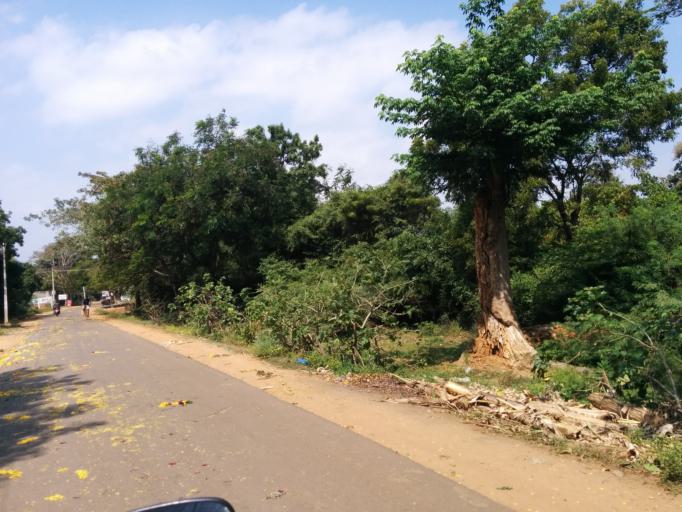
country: IN
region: Tamil Nadu
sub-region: Villupuram
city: Auroville
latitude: 11.9990
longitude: 79.8013
